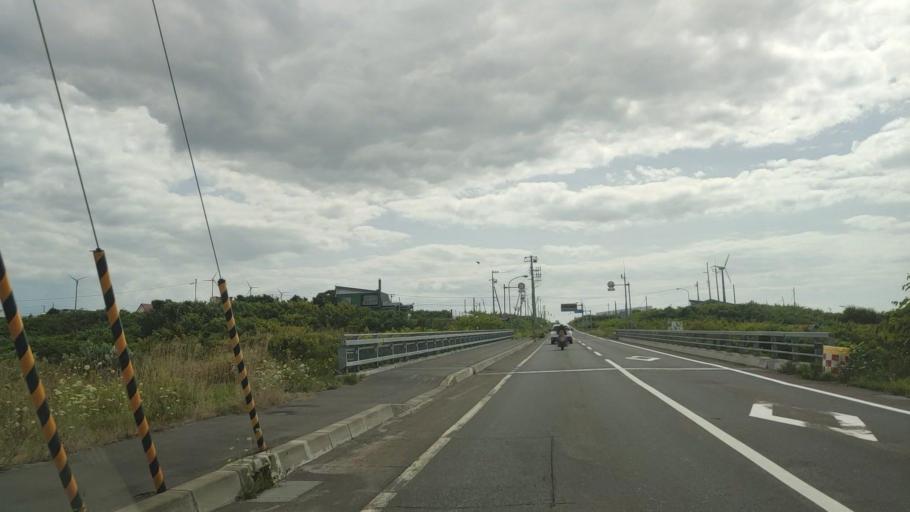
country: JP
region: Hokkaido
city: Rumoi
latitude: 44.5306
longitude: 141.7664
